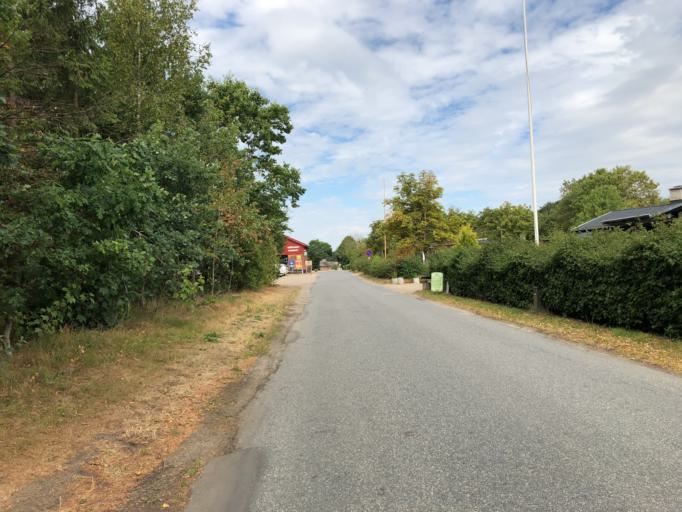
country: DK
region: South Denmark
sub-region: Vejle Kommune
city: Egtved
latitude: 55.6559
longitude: 9.2609
